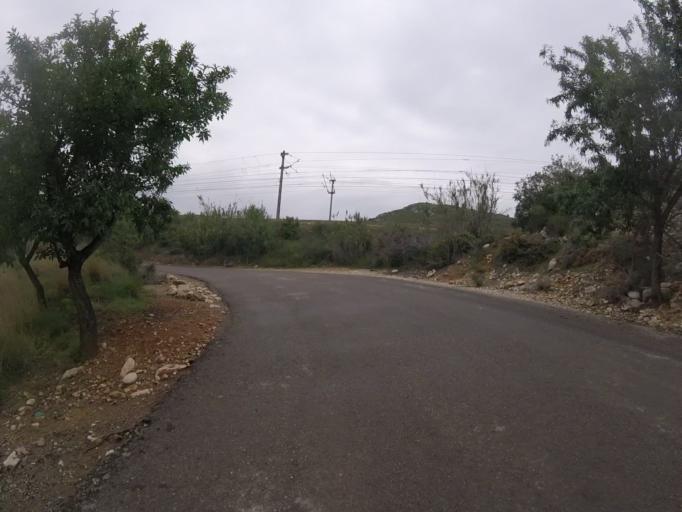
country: ES
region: Valencia
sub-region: Provincia de Castello
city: Alcala de Xivert
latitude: 40.2732
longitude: 0.2426
